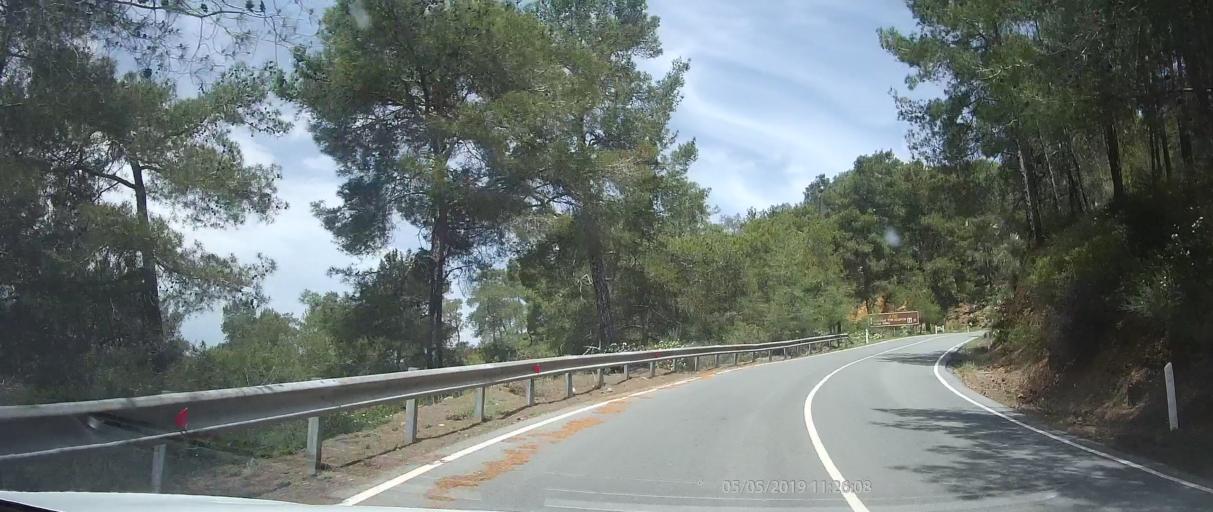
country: CY
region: Limassol
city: Pachna
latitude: 34.9268
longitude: 32.6473
